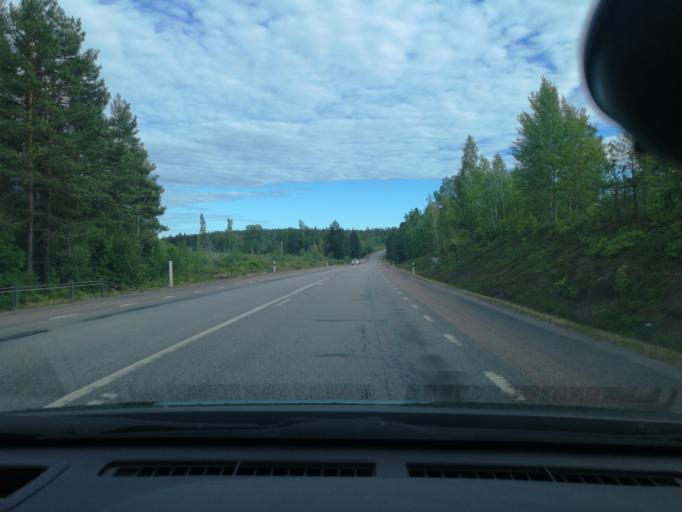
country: SE
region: Kalmar
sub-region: Vasterviks Kommun
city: Ankarsrum
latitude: 57.6341
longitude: 16.4543
